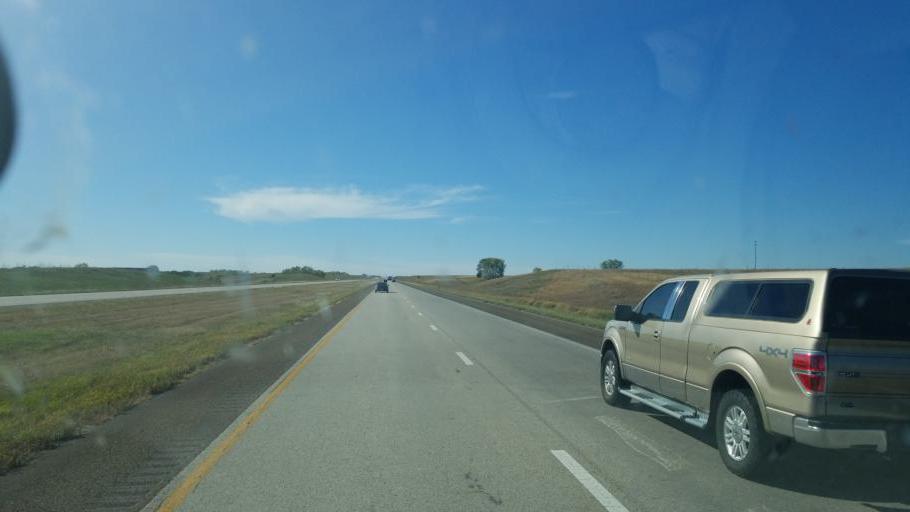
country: US
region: Kansas
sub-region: Saline County
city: Salina
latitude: 38.8779
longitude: -97.8307
